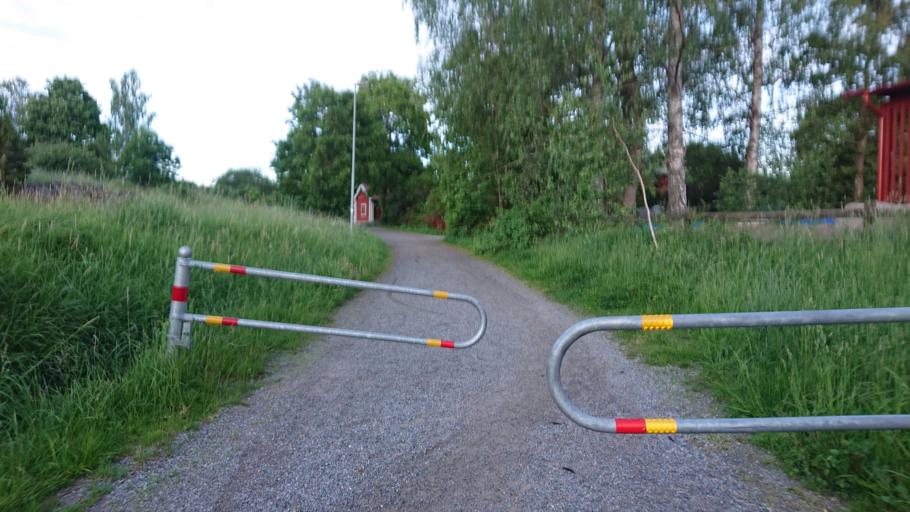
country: SE
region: Stockholm
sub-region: Osterakers Kommun
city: Akersberga
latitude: 59.5031
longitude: 18.3077
